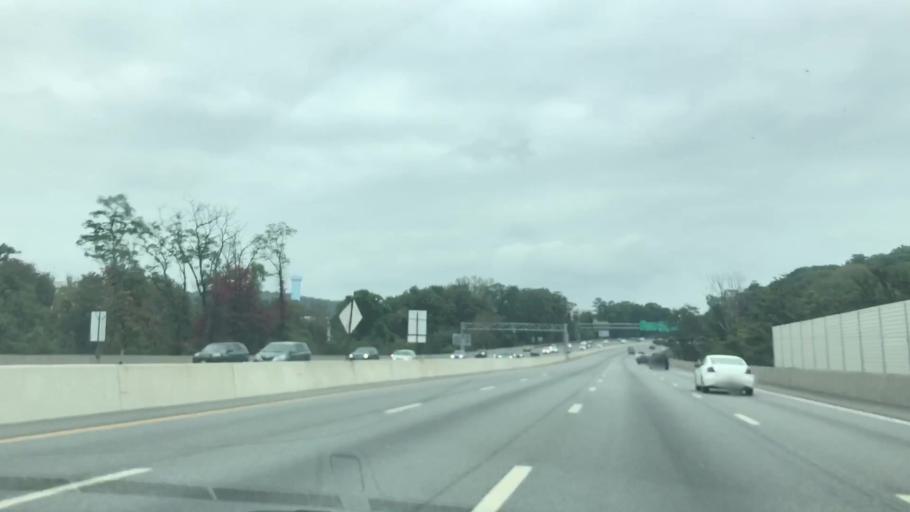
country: US
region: New York
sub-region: Westchester County
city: Tarrytown
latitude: 41.0607
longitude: -73.8478
